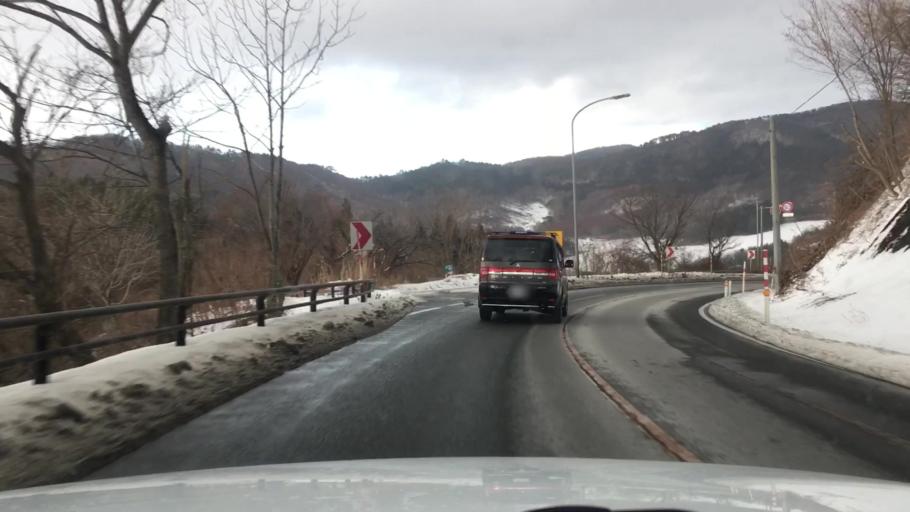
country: JP
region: Iwate
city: Morioka-shi
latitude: 39.6639
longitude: 141.3268
